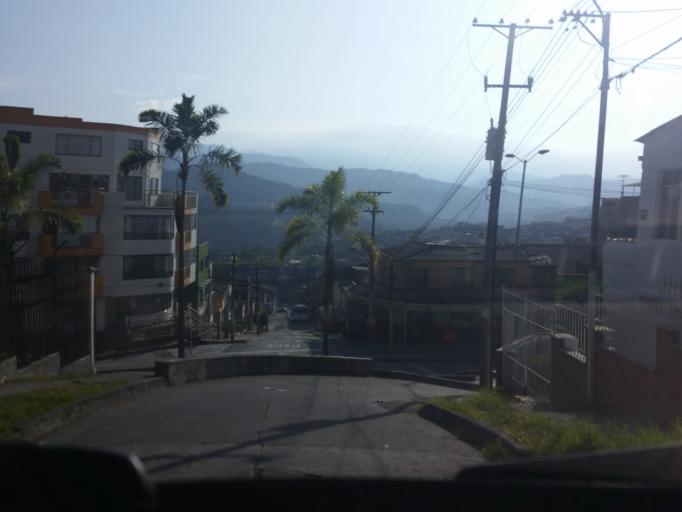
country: CO
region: Caldas
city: Manizales
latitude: 5.0748
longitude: -75.5210
